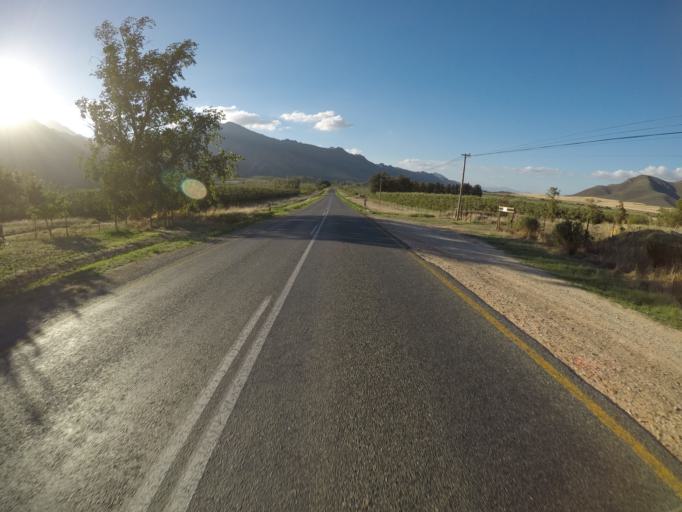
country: ZA
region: Western Cape
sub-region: Cape Winelands District Municipality
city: Worcester
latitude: -33.8866
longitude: 19.3645
